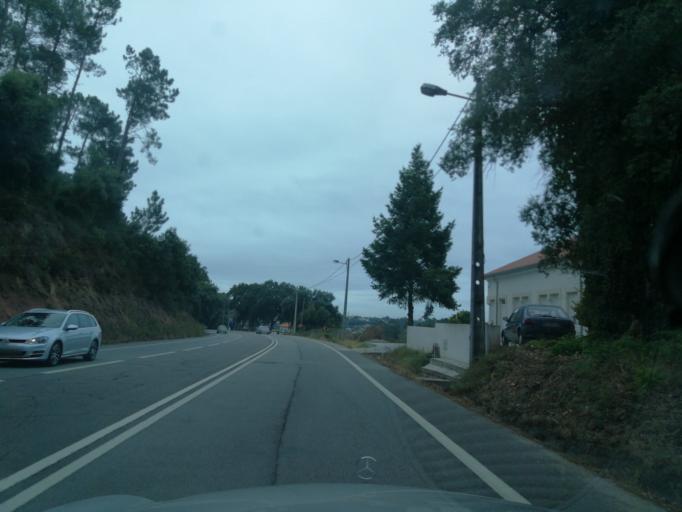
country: PT
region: Aveiro
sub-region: Agueda
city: Agueda
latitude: 40.5836
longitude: -8.4501
